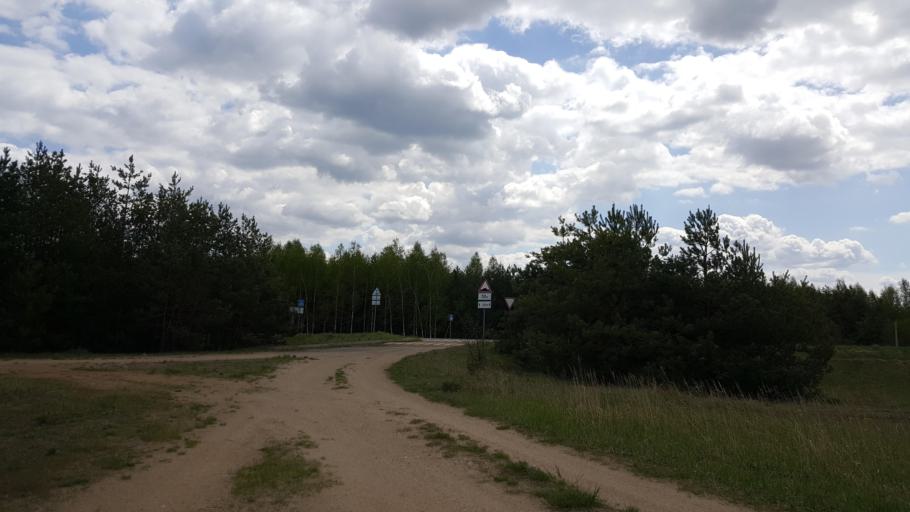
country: BY
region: Brest
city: Zhabinka
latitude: 52.3995
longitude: 24.0673
